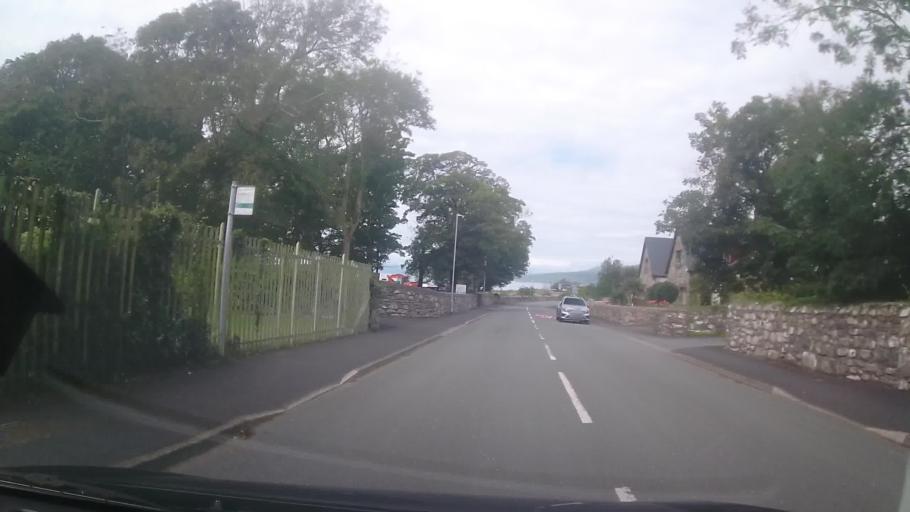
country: GB
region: Wales
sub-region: Gwynedd
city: Barmouth
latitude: 52.6680
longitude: -4.0841
